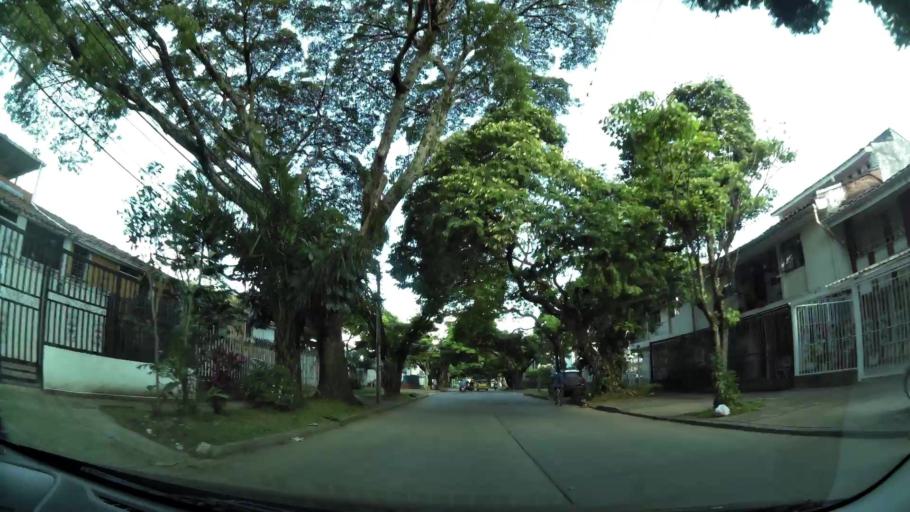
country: CO
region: Valle del Cauca
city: Cali
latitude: 3.4208
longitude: -76.5508
